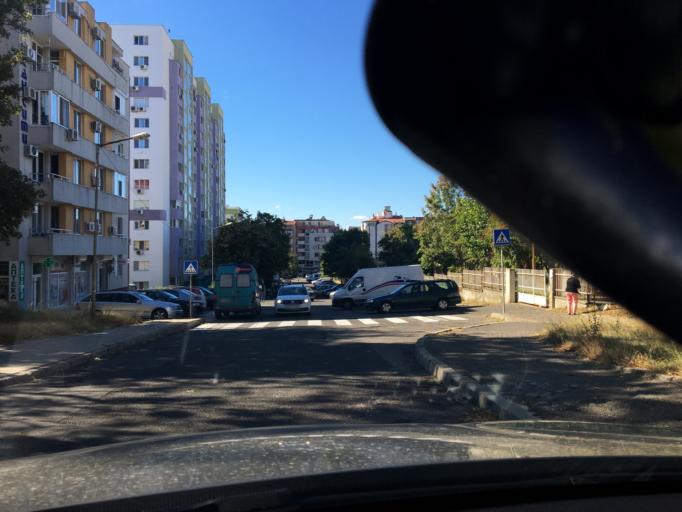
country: BG
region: Burgas
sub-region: Obshtina Burgas
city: Burgas
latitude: 42.5155
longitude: 27.4584
